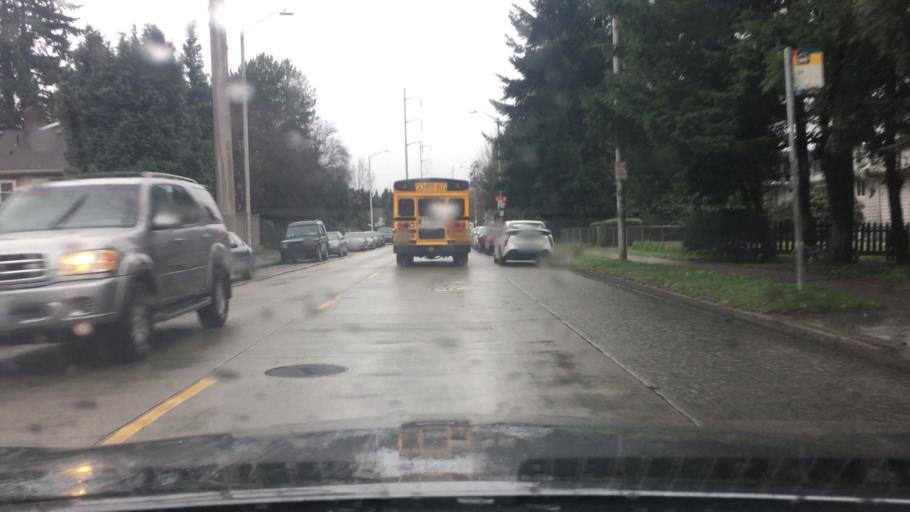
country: US
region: Washington
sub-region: King County
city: White Center
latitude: 47.5280
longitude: -122.3605
